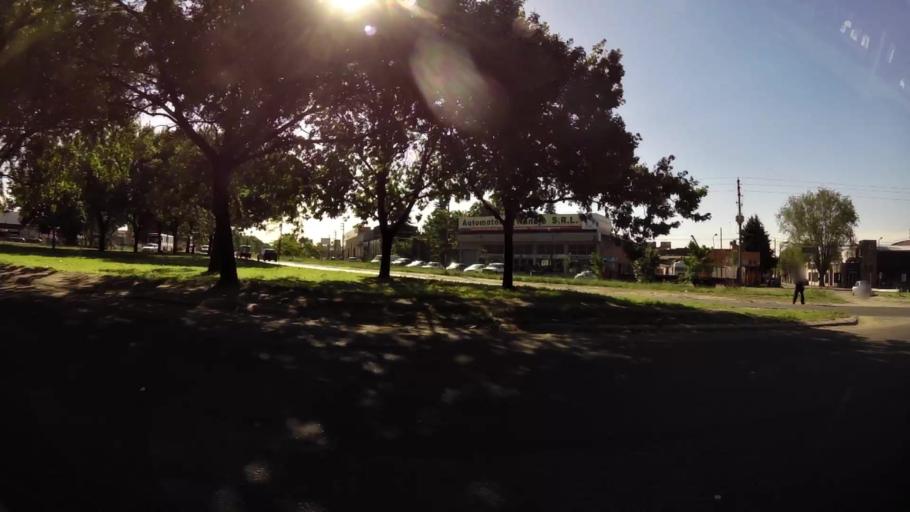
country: AR
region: Buenos Aires
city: Caseros
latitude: -34.5624
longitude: -58.5889
